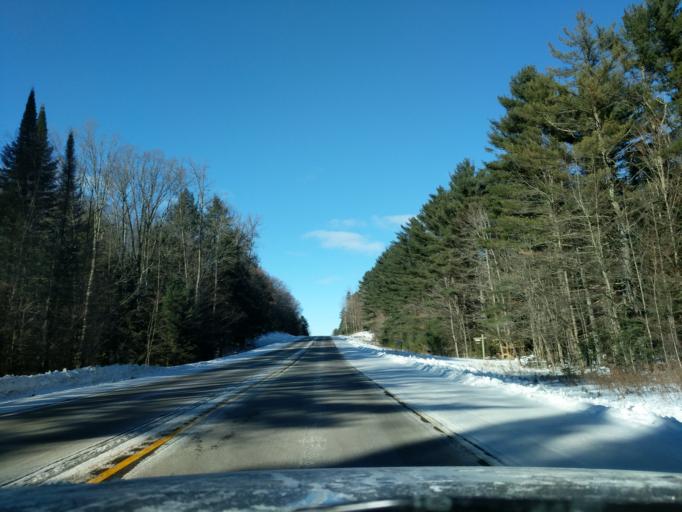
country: US
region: Wisconsin
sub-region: Menominee County
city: Keshena
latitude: 45.1321
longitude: -88.6710
